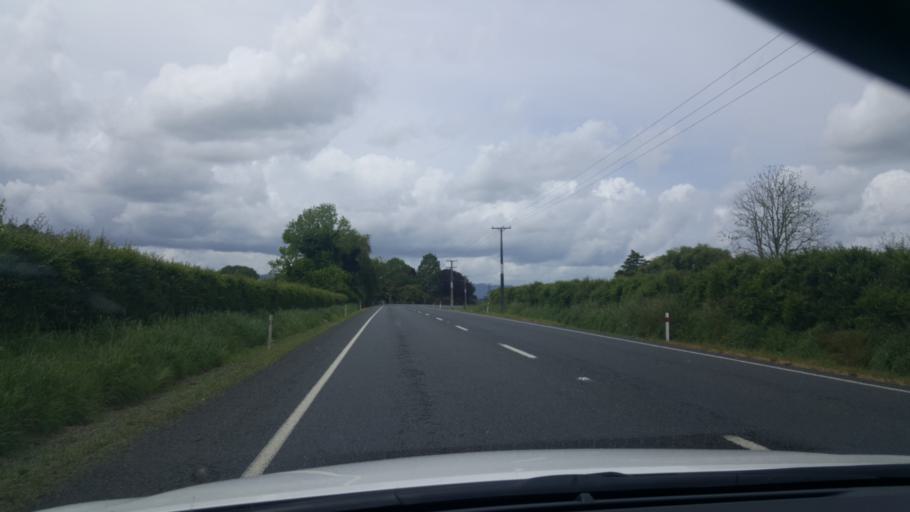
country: NZ
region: Waikato
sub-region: Matamata-Piako District
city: Matamata
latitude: -37.8797
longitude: 175.7508
